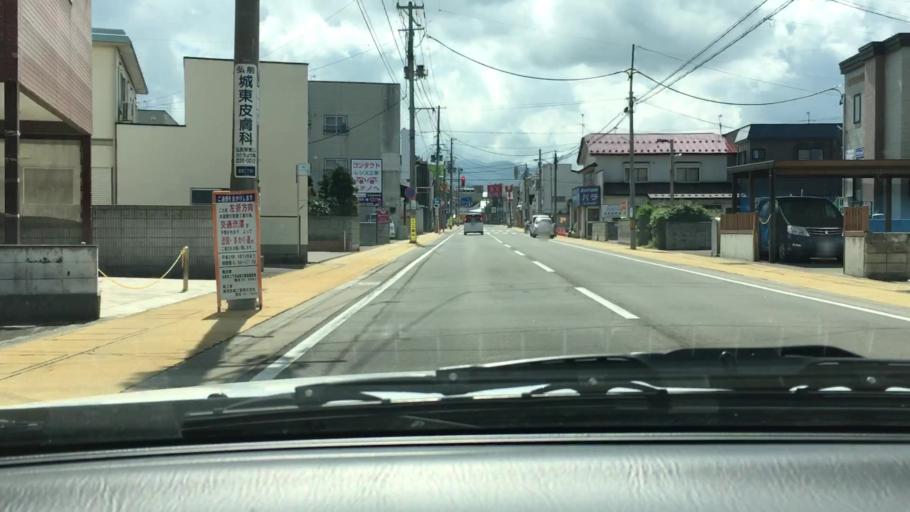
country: JP
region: Aomori
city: Hirosaki
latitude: 40.5941
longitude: 140.4735
